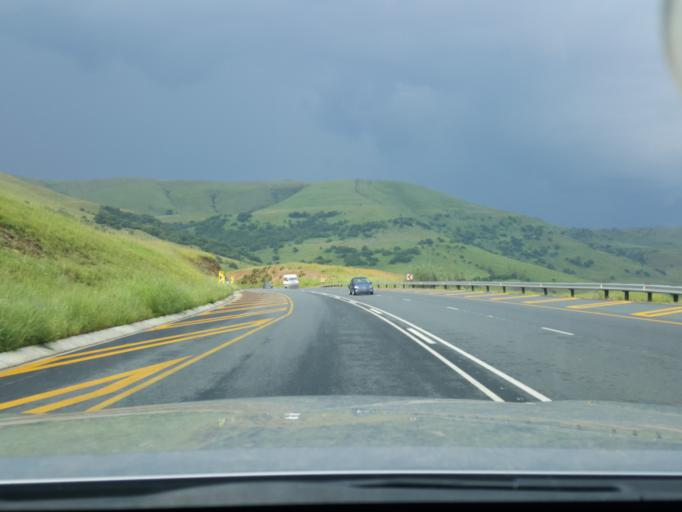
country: ZA
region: Mpumalanga
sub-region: Nkangala District Municipality
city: Belfast
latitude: -25.6299
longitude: 30.3254
